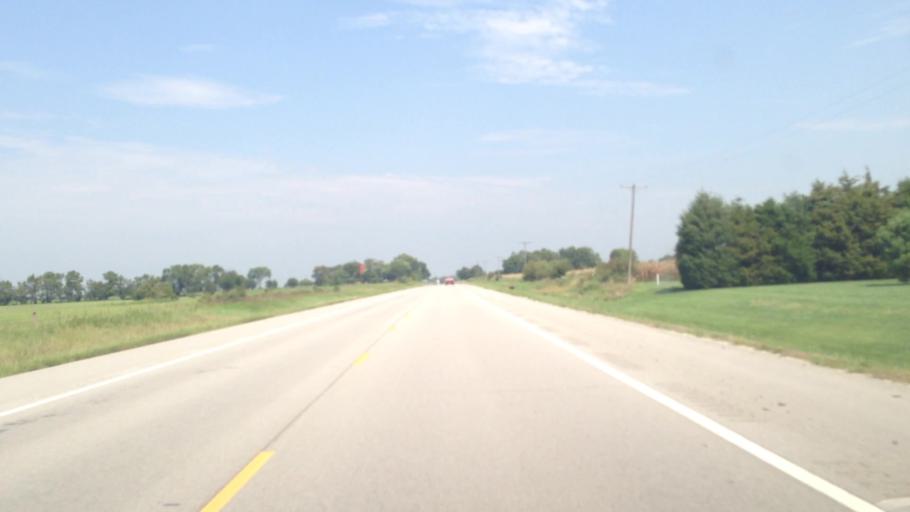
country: US
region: Kansas
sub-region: Labette County
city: Altamont
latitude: 37.2375
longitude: -95.2672
